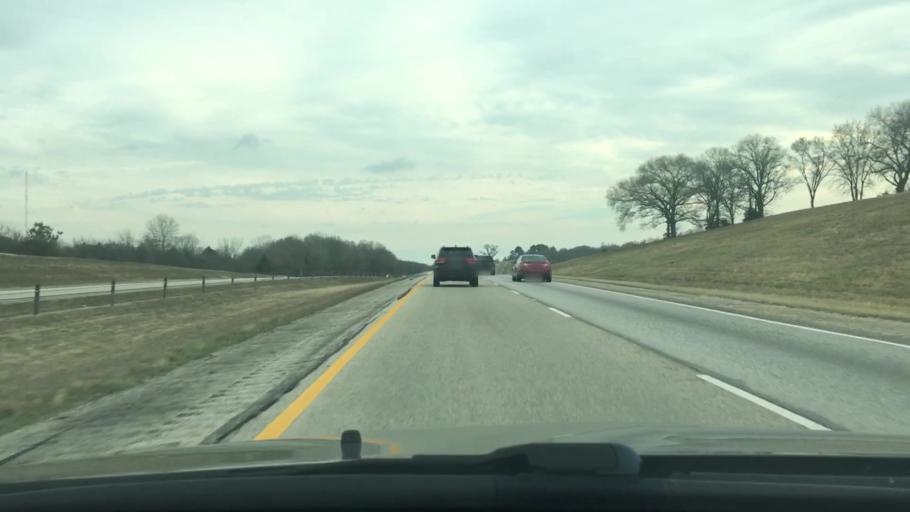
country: US
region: Texas
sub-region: Leon County
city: Centerville
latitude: 31.2877
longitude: -95.9948
